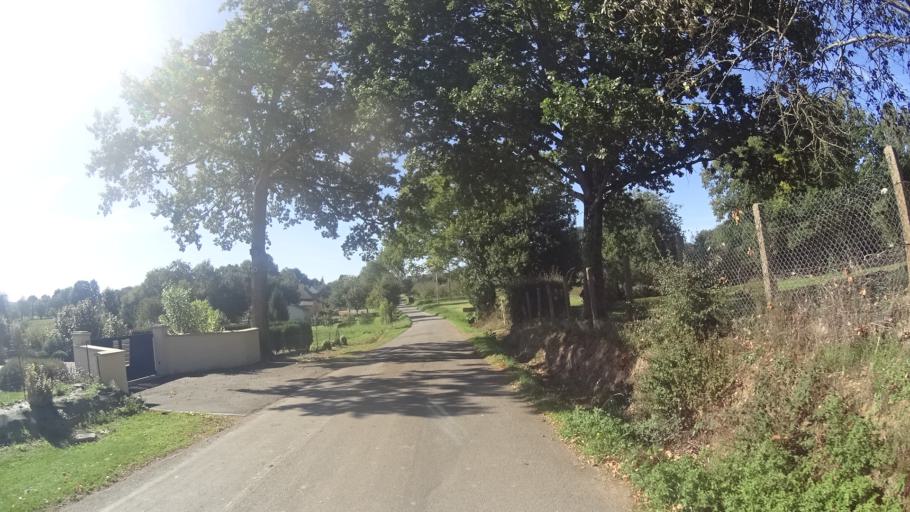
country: FR
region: Brittany
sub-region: Departement du Morbihan
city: Peillac
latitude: 47.7405
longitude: -2.2079
